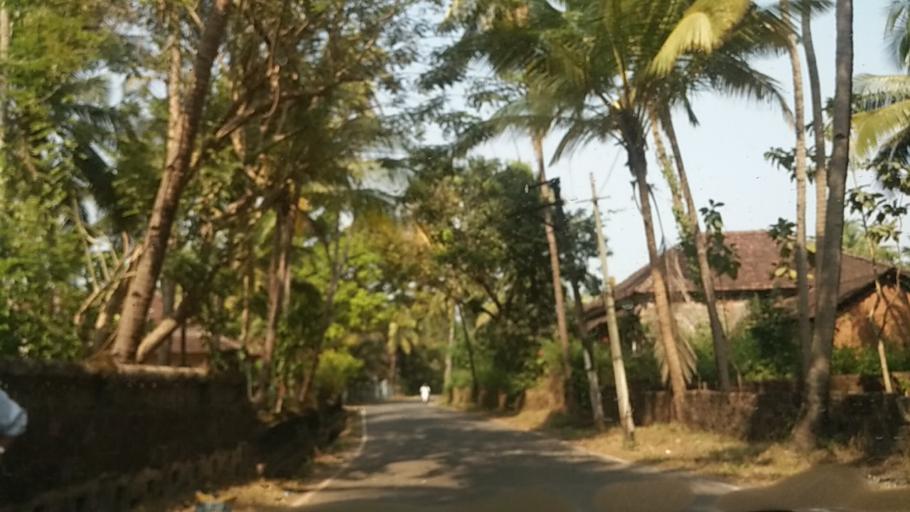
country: IN
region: Goa
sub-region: South Goa
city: Cavelossim
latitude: 15.1544
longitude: 73.9652
